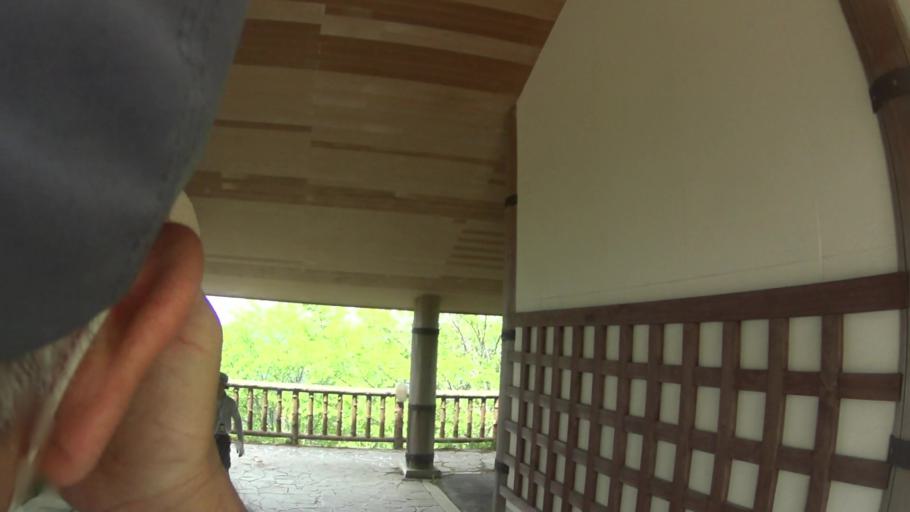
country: JP
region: Nara
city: Yoshino-cho
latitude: 34.3504
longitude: 135.8781
